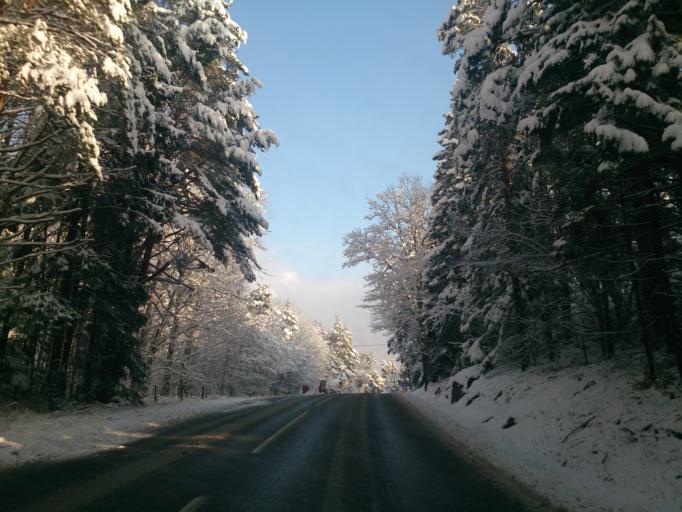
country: SE
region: Stockholm
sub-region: Varmdo Kommun
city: Holo
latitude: 59.2830
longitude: 18.6371
